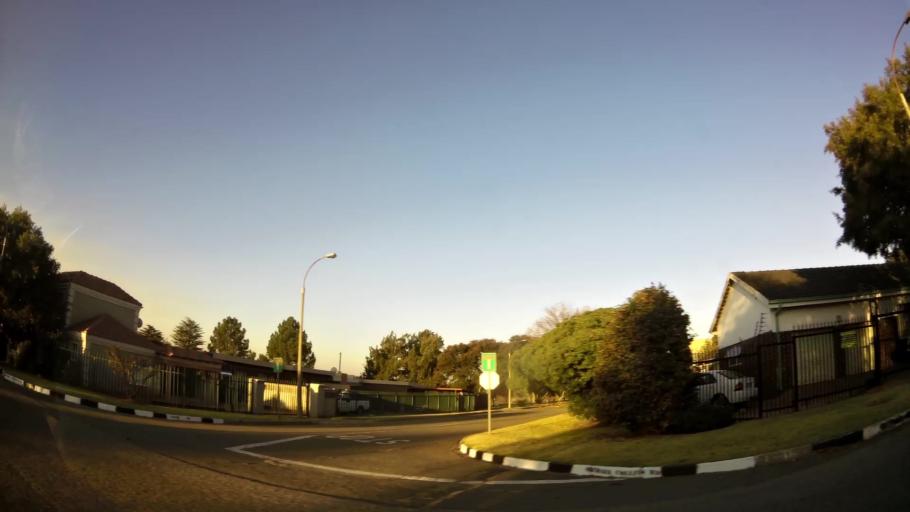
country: ZA
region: Gauteng
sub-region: City of Johannesburg Metropolitan Municipality
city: Roodepoort
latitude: -26.1533
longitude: 27.8991
